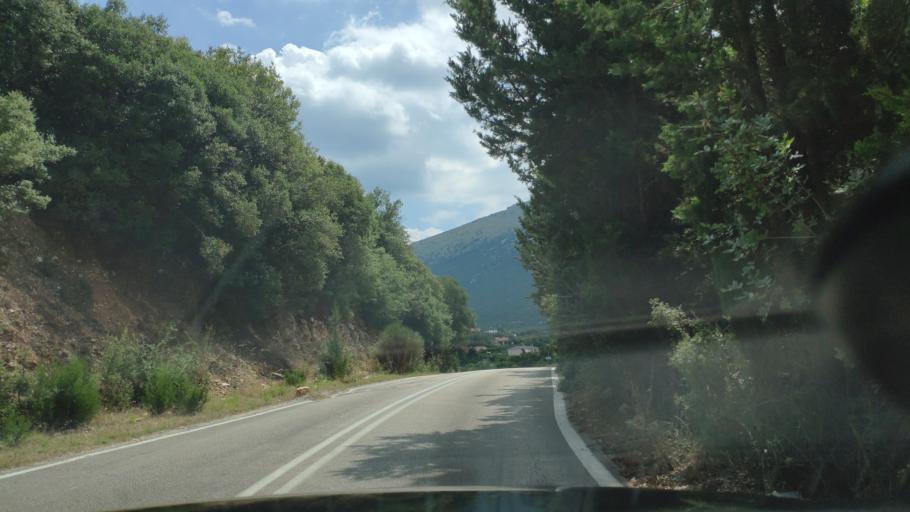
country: GR
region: Epirus
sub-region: Nomos Artas
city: Kampi
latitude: 39.2731
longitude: 20.9355
